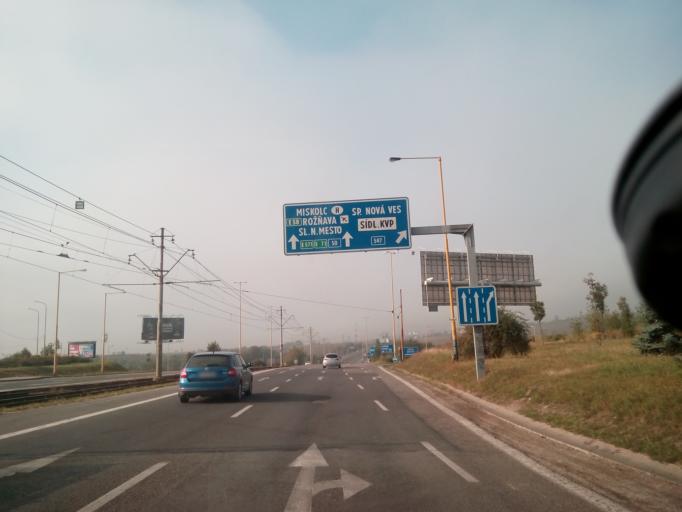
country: SK
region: Kosicky
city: Kosice
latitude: 48.6967
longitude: 21.2355
